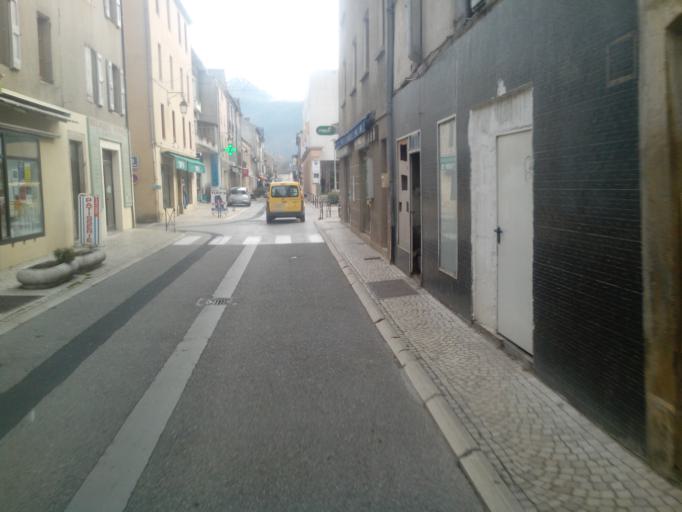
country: FR
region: Languedoc-Roussillon
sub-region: Departement de la Lozere
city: Florac
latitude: 44.3259
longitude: 3.5941
